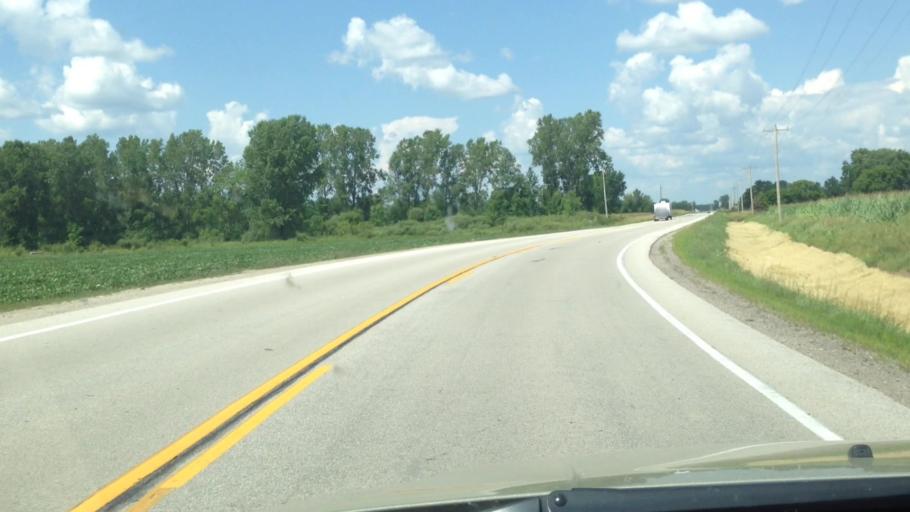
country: US
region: Wisconsin
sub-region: Brown County
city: Pulaski
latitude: 44.6464
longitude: -88.1807
